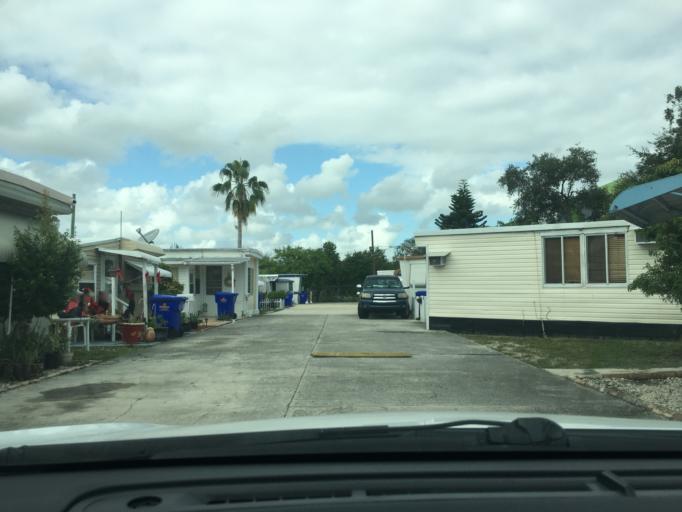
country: US
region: Florida
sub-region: Broward County
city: Dania Beach
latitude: 26.0641
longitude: -80.1717
